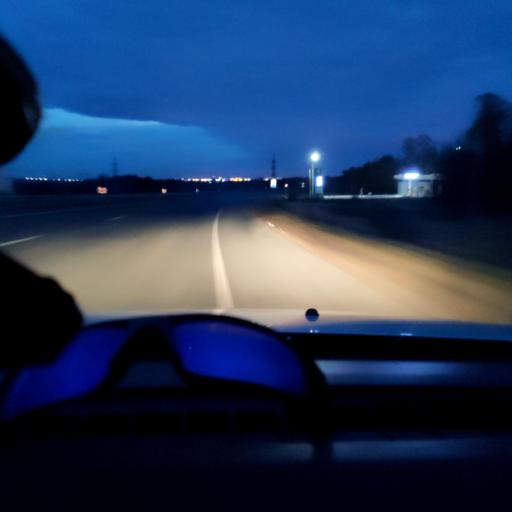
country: RU
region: Samara
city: Novokuybyshevsk
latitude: 53.0225
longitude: 49.9845
